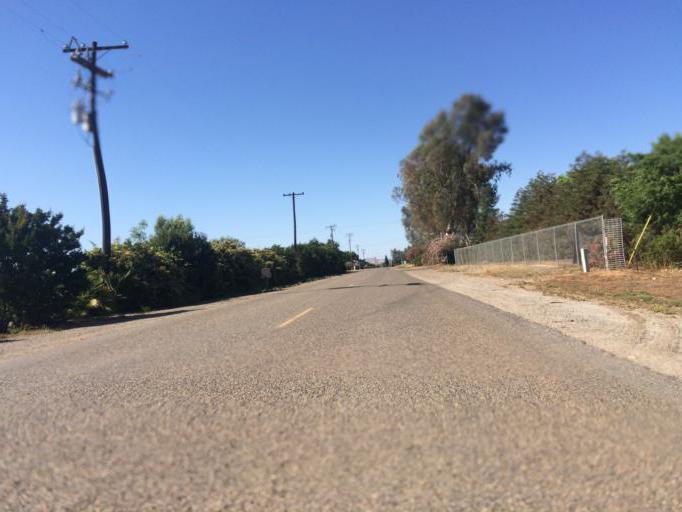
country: US
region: California
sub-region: Fresno County
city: Tarpey Village
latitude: 36.7891
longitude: -119.6279
